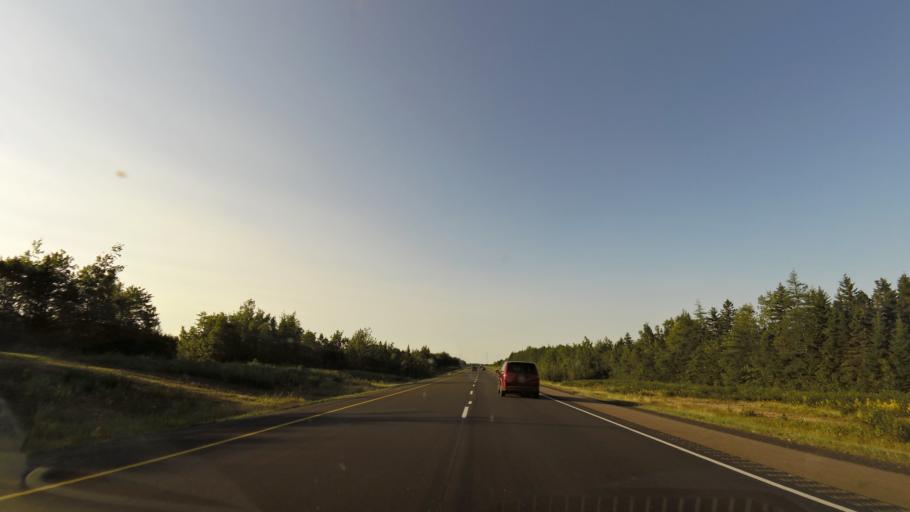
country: CA
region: New Brunswick
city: Dieppe
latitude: 46.0568
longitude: -64.5866
